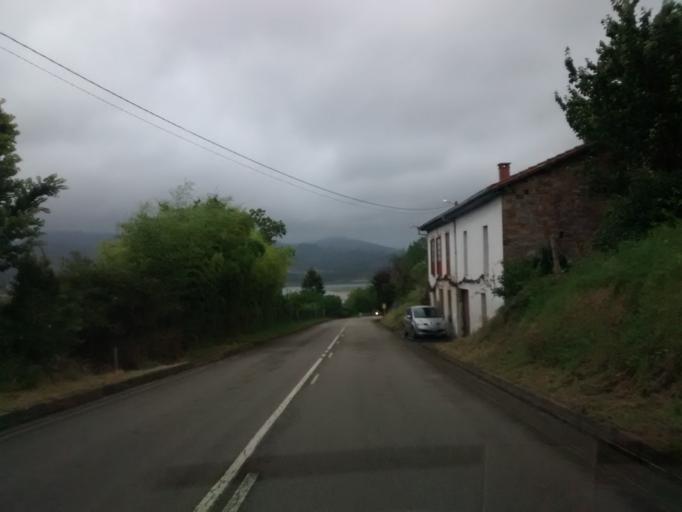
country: ES
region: Asturias
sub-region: Province of Asturias
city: Villaviciosa
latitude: 43.5284
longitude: -5.3901
